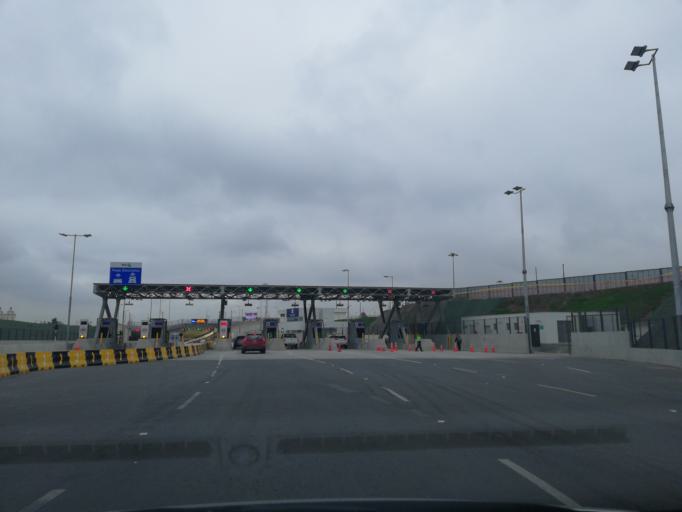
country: PE
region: Lima
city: Lima
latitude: -12.0434
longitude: -77.0195
